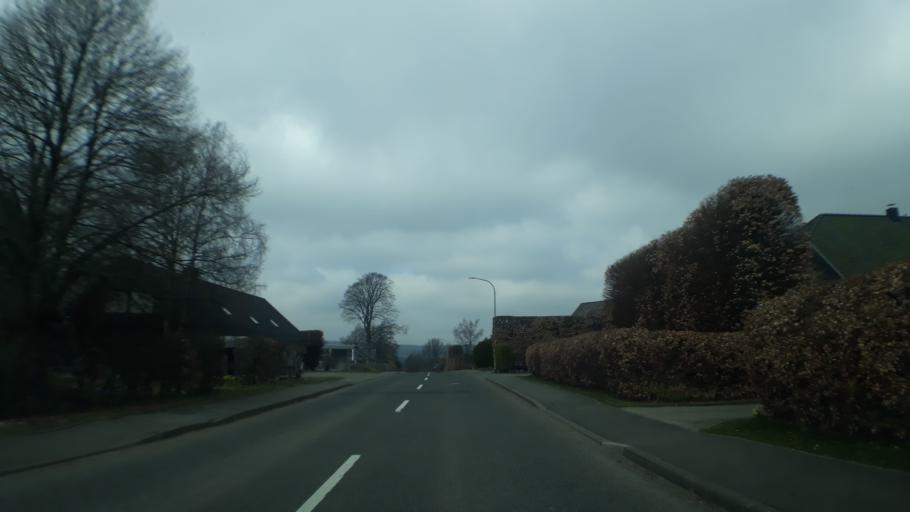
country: DE
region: North Rhine-Westphalia
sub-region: Regierungsbezirk Koln
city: Monschau
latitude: 50.5327
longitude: 6.2116
